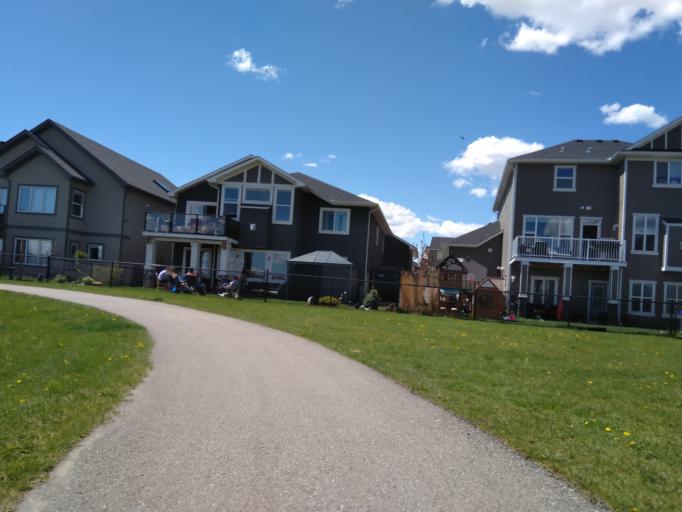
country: CA
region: Alberta
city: Chestermere
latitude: 51.0215
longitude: -113.8362
